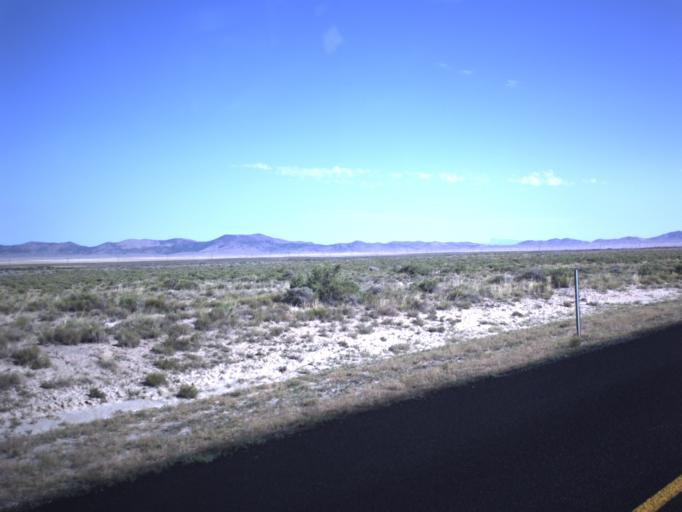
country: US
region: Utah
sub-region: Beaver County
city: Milford
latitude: 38.5299
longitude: -112.9912
